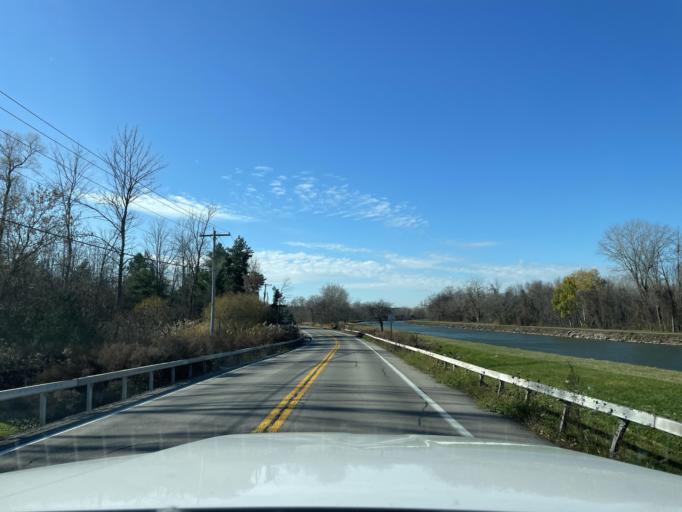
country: US
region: New York
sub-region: Orleans County
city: Medina
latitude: 43.2156
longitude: -78.4314
